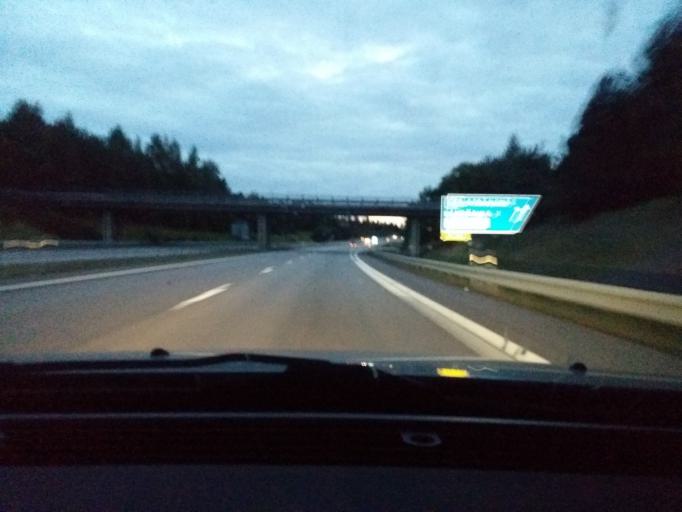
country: SE
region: Uppsala
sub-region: Enkopings Kommun
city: Enkoping
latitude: 59.6486
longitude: 17.0607
